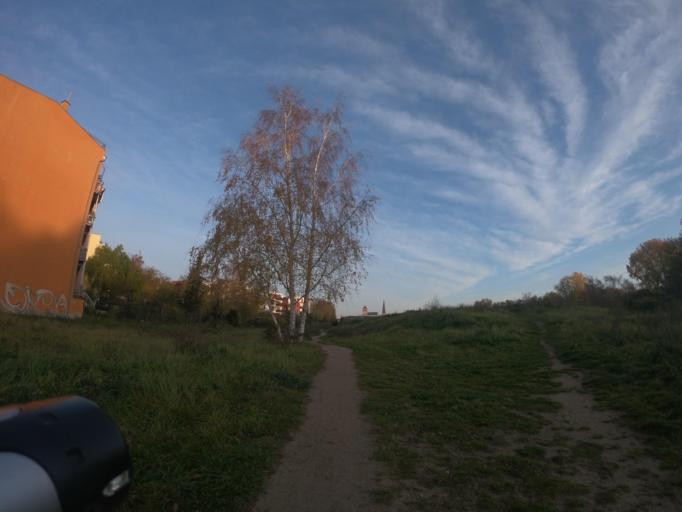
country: DE
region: Mecklenburg-Vorpommern
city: Rostock
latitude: 54.0784
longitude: 12.1460
